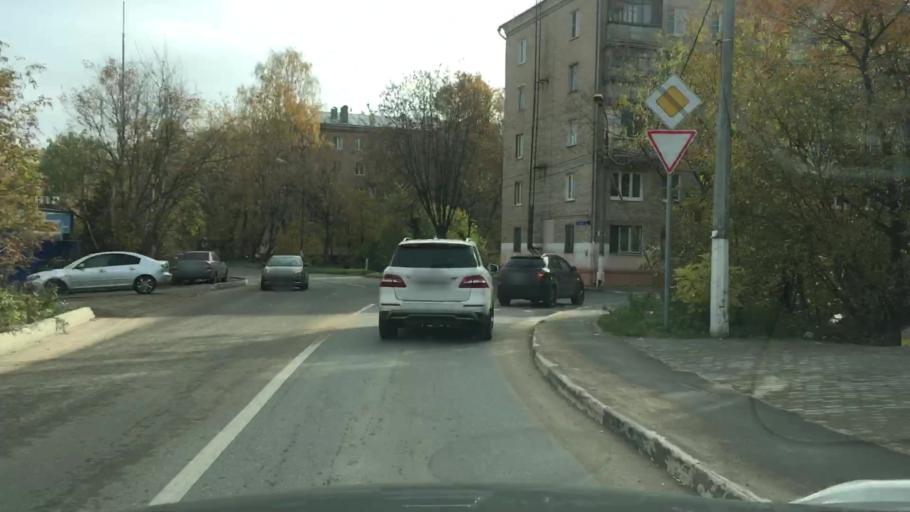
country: RU
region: Moskovskaya
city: Balashikha
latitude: 55.8041
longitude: 37.9268
